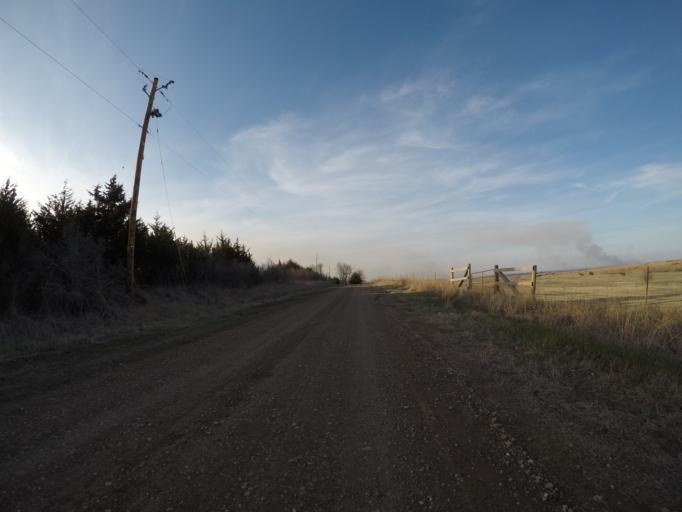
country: US
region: Kansas
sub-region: Riley County
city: Manhattan
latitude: 39.2527
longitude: -96.6584
